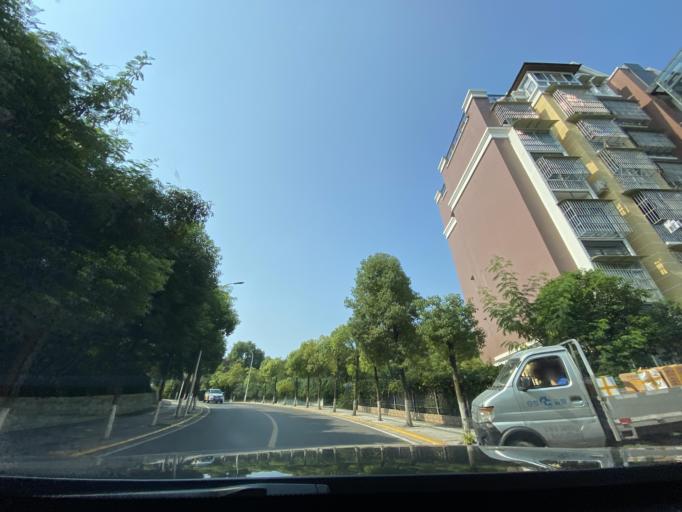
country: CN
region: Sichuan
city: Jiancheng
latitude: 30.4198
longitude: 104.5445
